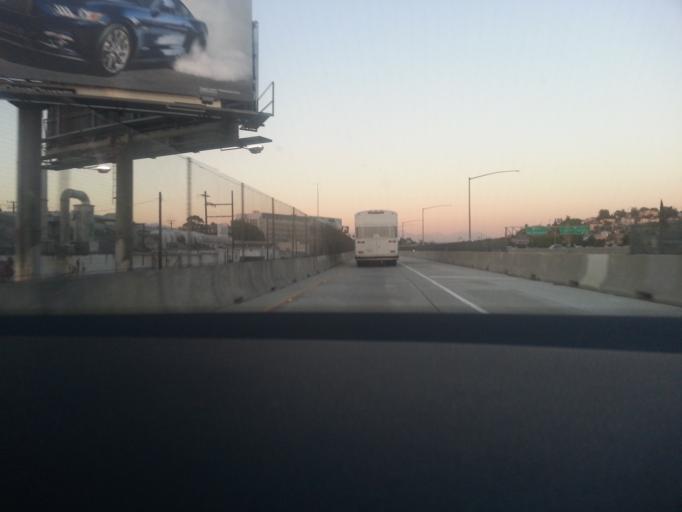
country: US
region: California
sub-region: Los Angeles County
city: Belvedere
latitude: 34.0588
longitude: -118.1784
